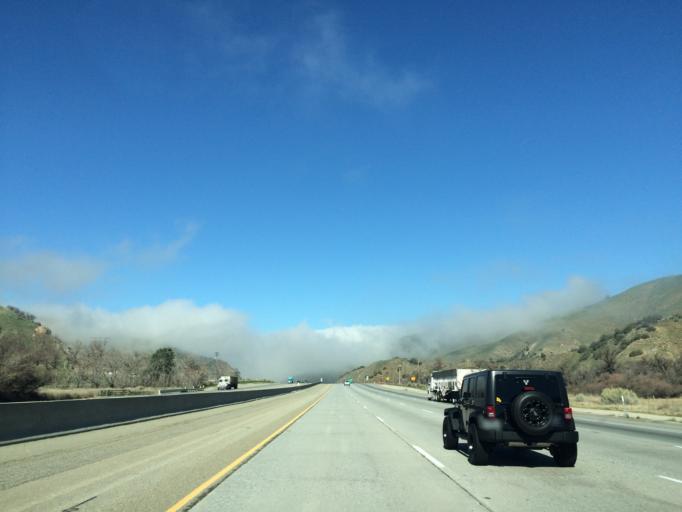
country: US
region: California
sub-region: Kern County
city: Lebec
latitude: 34.8582
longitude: -118.8765
